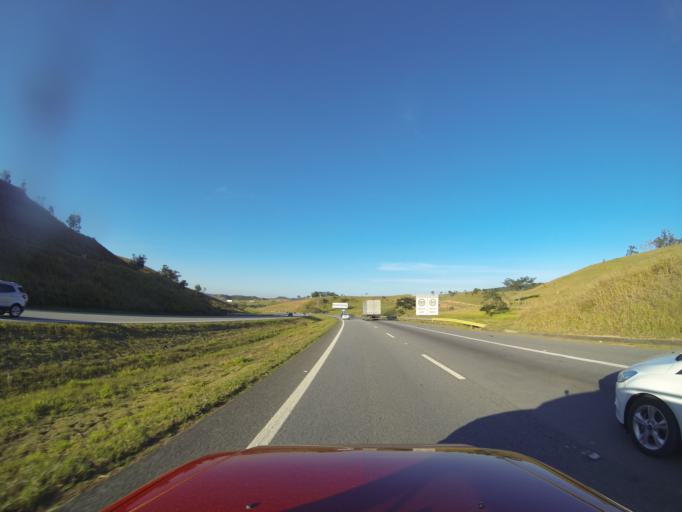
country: BR
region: Sao Paulo
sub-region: Jacarei
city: Jacarei
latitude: -23.3161
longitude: -45.9035
